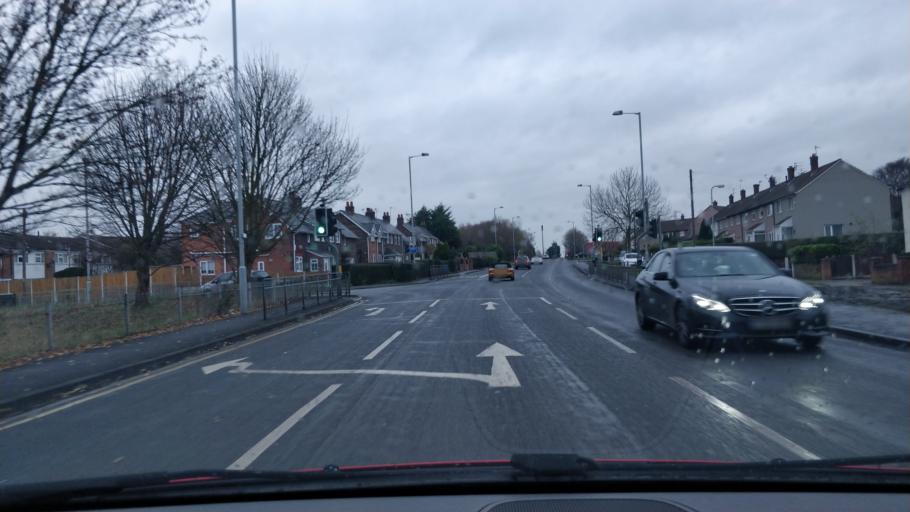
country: GB
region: England
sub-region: Sefton
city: Thornton
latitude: 53.4871
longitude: -2.9923
